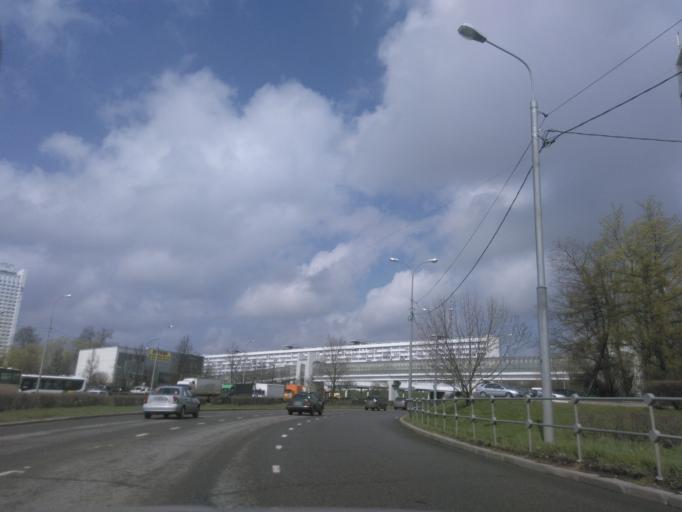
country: RU
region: Moskovskaya
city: Rzhavki
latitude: 55.9891
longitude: 37.2254
